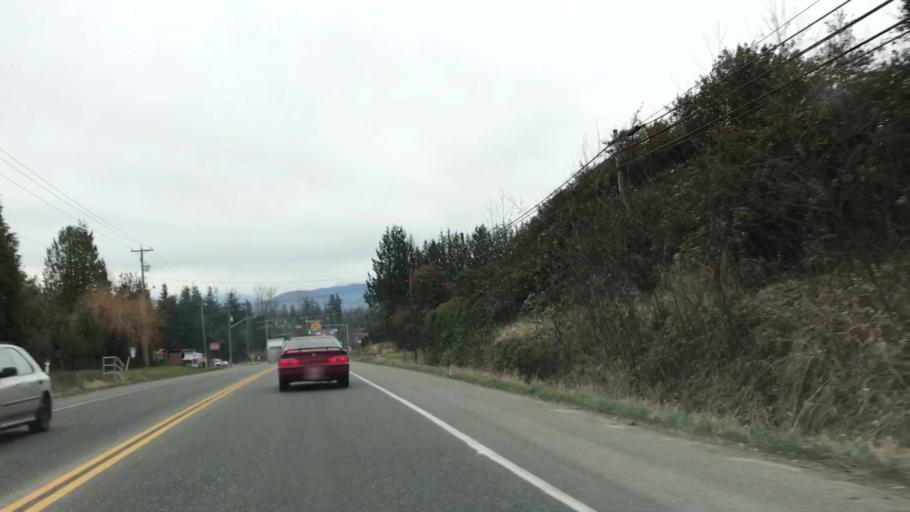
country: CA
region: British Columbia
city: Aldergrove
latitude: 49.0575
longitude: -122.4080
